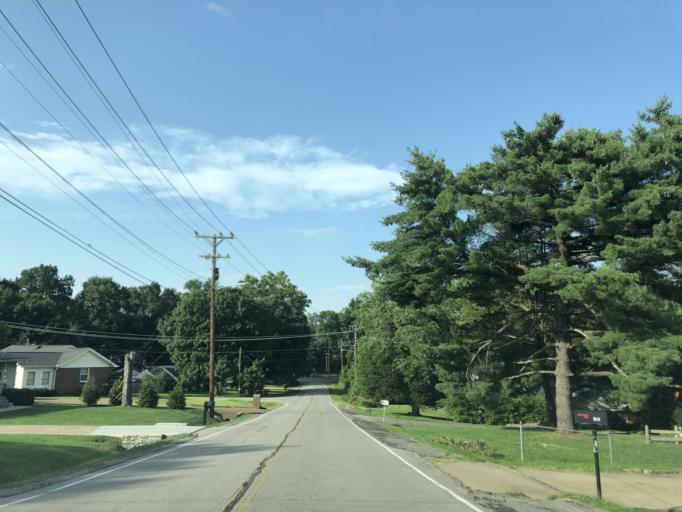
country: US
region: Tennessee
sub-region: Davidson County
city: Lakewood
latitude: 36.1514
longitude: -86.6545
